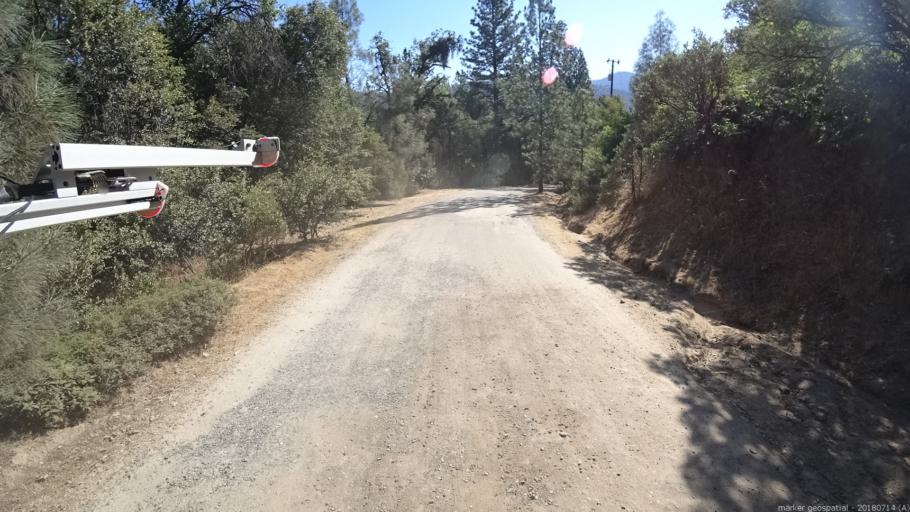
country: US
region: California
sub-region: Madera County
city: Oakhurst
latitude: 37.3869
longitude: -119.6355
